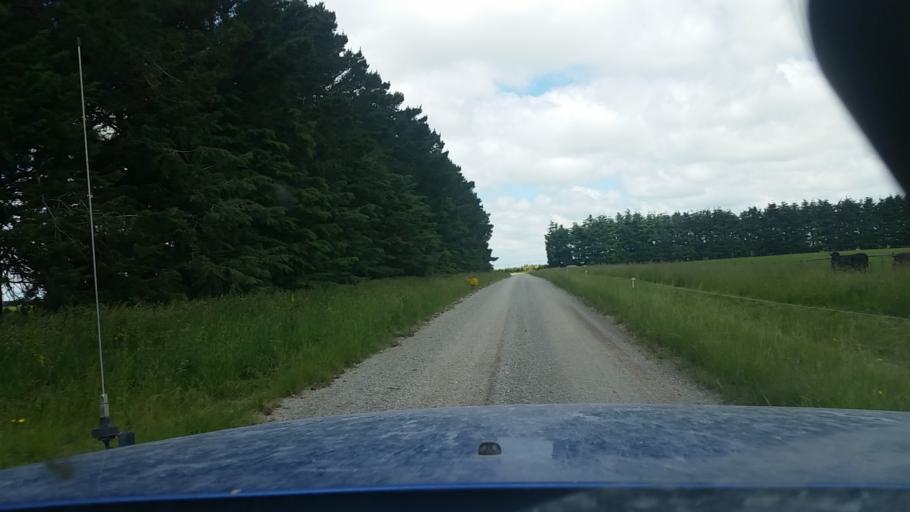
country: NZ
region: Canterbury
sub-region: Ashburton District
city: Tinwald
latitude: -43.8809
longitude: 171.3306
